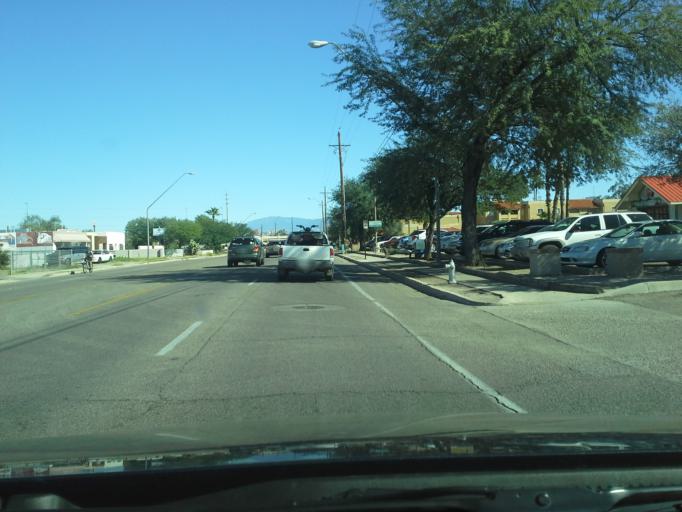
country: US
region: Arizona
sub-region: Pima County
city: South Tucson
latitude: 32.2298
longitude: -110.9878
